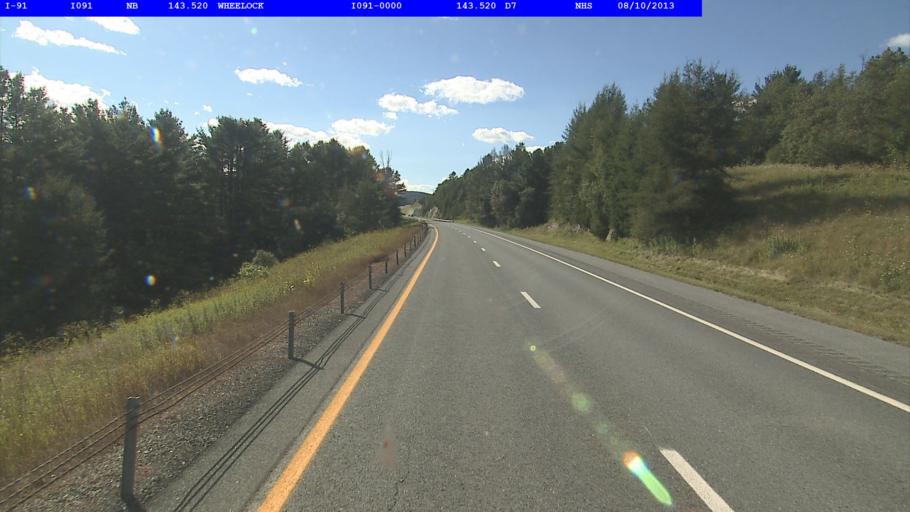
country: US
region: Vermont
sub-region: Caledonia County
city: Lyndonville
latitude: 44.5877
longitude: -72.0761
